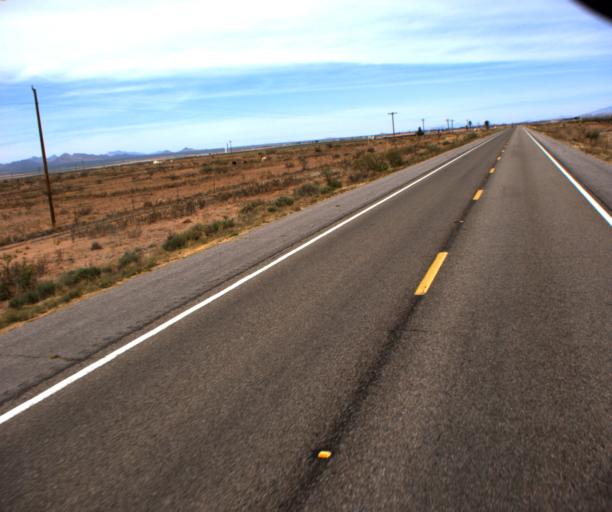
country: US
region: Arizona
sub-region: Cochise County
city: Pirtleville
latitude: 31.6250
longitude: -109.6715
